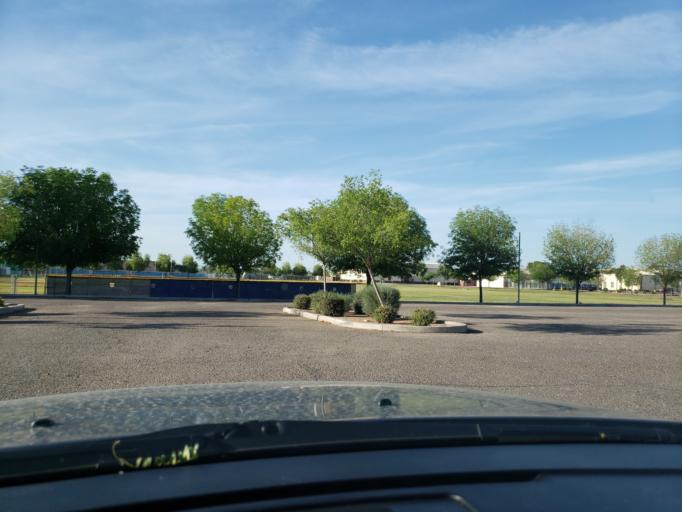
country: US
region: Arizona
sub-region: Maricopa County
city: Chandler
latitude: 33.3064
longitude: -111.8453
